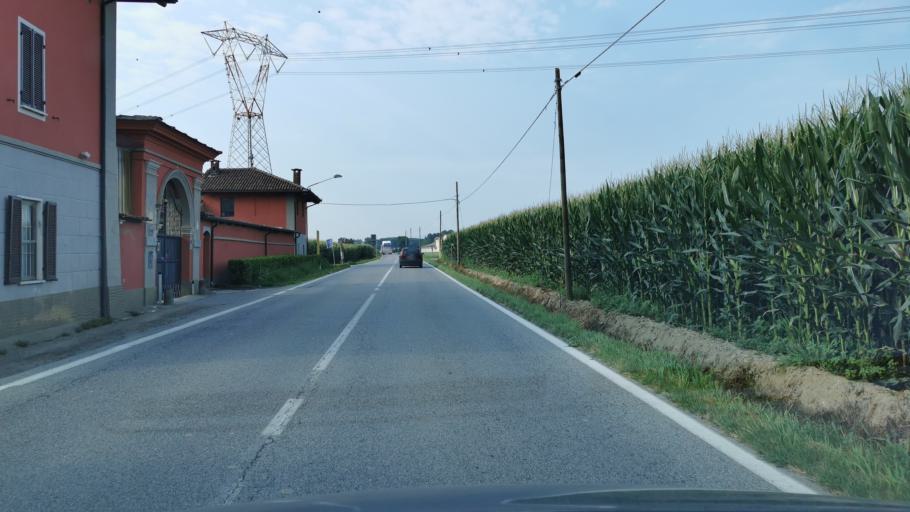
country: IT
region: Piedmont
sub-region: Provincia di Torino
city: Scalenghe
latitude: 44.8816
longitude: 7.4948
